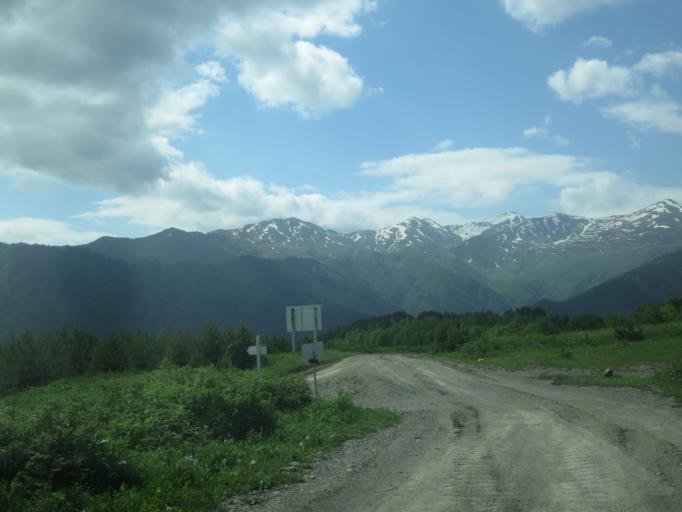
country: RU
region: Chechnya
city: Itum-Kali
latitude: 42.3684
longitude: 45.6269
